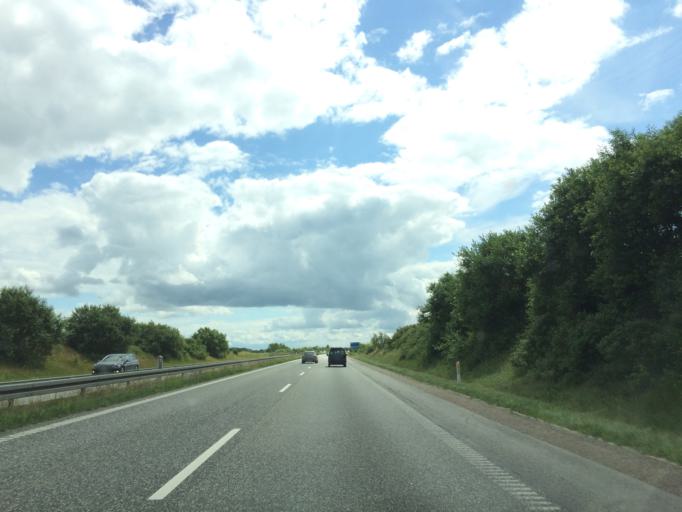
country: DK
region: North Denmark
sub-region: Mariagerfjord Kommune
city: Hobro
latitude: 56.6836
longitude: 9.7314
